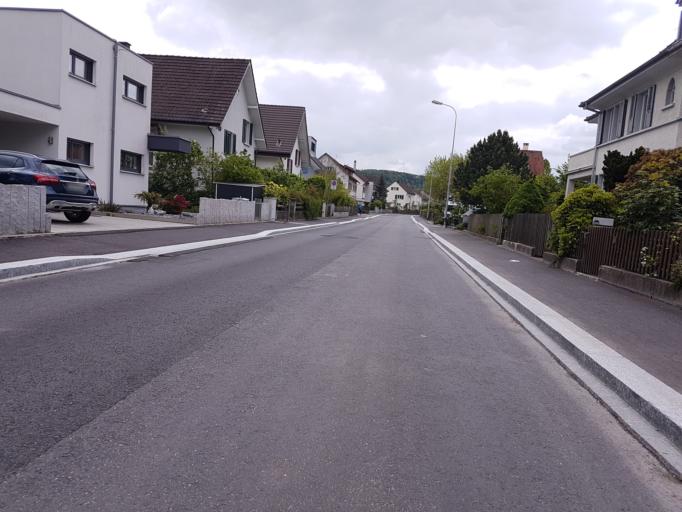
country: CH
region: Aargau
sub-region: Bezirk Brugg
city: Brugg
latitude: 47.4818
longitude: 8.2016
